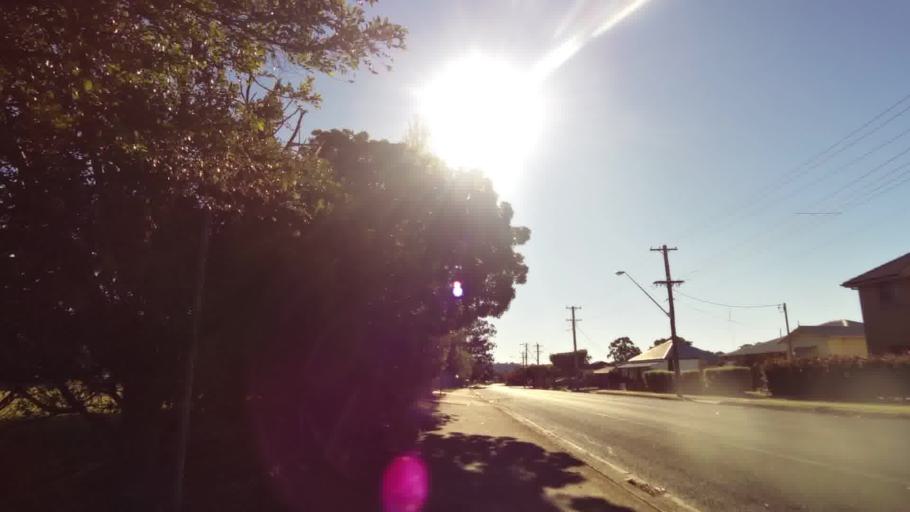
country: AU
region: New South Wales
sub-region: Wollongong
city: Dapto
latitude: -34.4910
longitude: 150.7938
